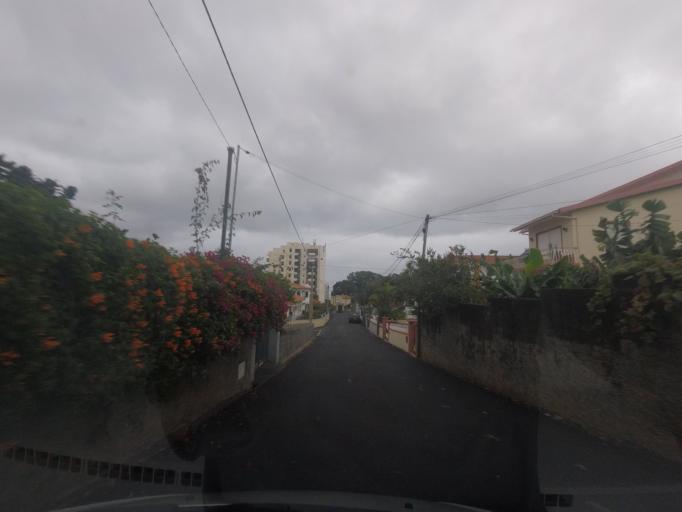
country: PT
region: Madeira
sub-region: Funchal
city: Nossa Senhora do Monte
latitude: 32.6515
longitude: -16.9339
